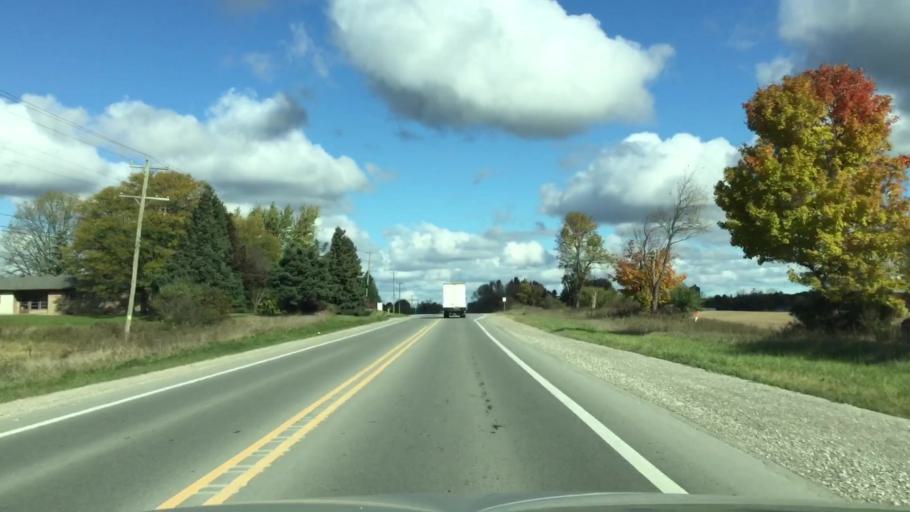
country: US
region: Michigan
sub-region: Oakland County
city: Oxford
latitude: 42.9021
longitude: -83.3119
